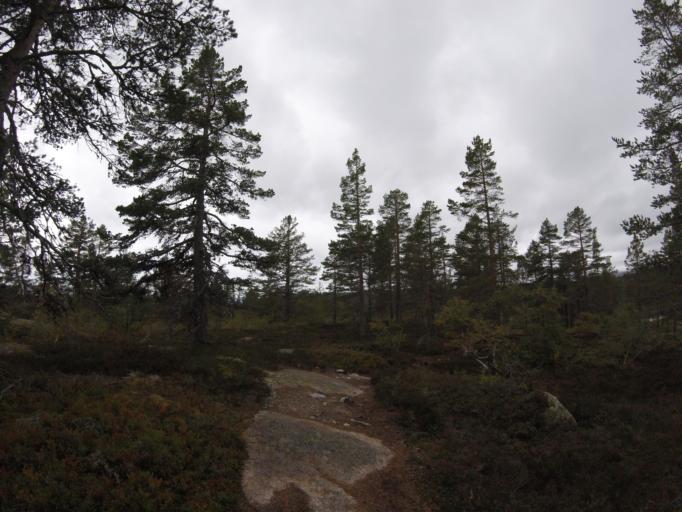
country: NO
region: Buskerud
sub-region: Flesberg
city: Lampeland
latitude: 59.7582
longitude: 9.3927
